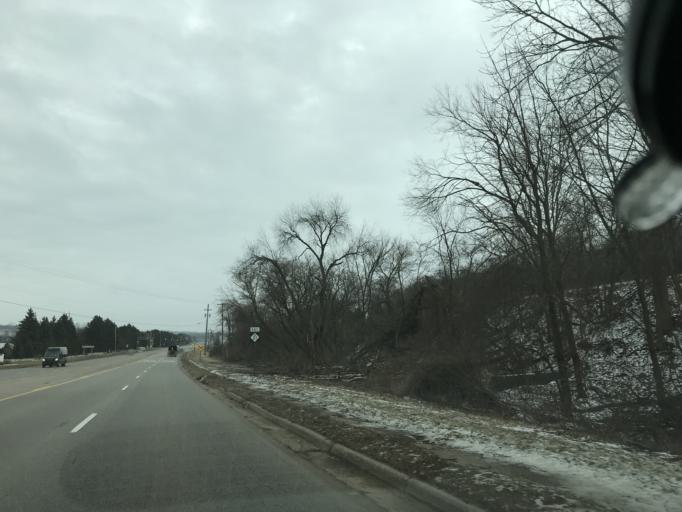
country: US
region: Michigan
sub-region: Kent County
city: Forest Hills
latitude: 42.9606
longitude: -85.5008
